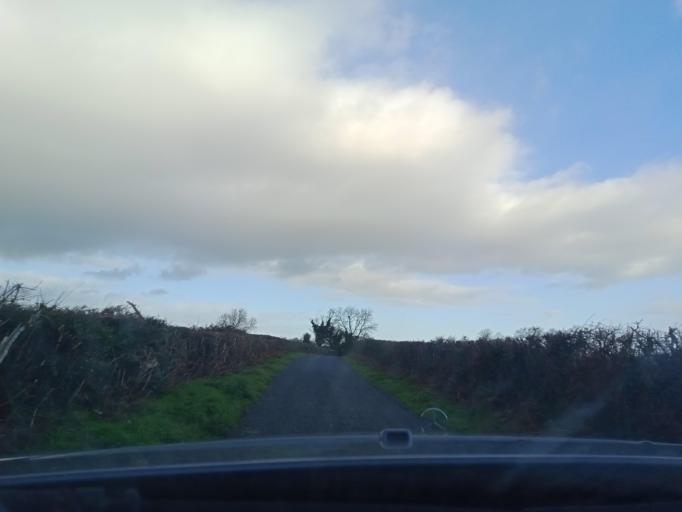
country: IE
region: Leinster
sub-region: Kilkenny
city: Callan
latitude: 52.4727
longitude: -7.3829
